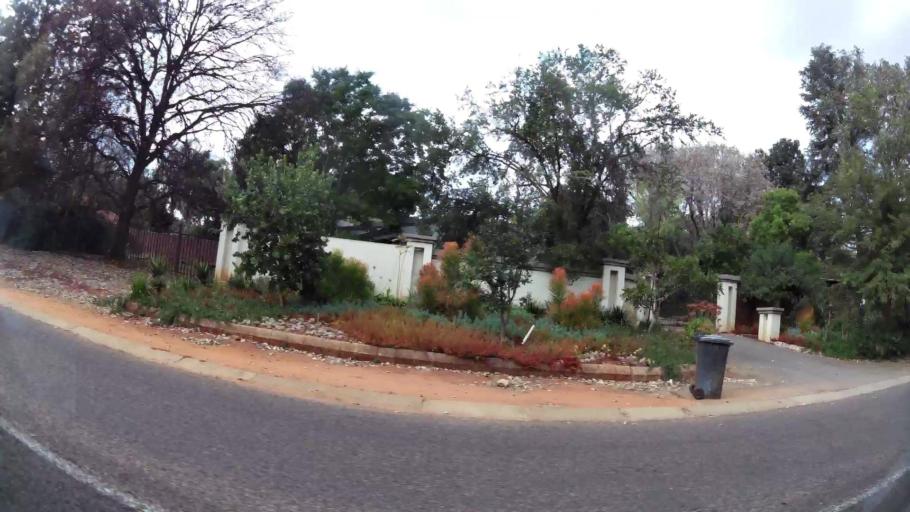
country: ZA
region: Gauteng
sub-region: City of Tshwane Metropolitan Municipality
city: Pretoria
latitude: -25.7549
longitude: 28.2959
